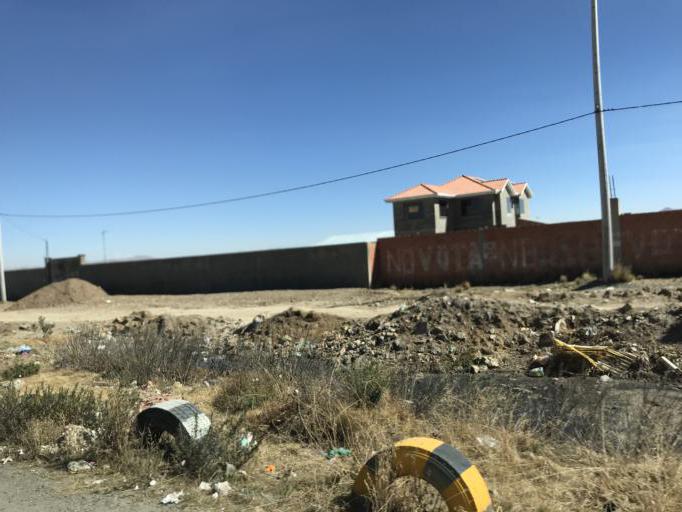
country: BO
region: La Paz
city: La Paz
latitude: -16.5132
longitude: -68.2764
